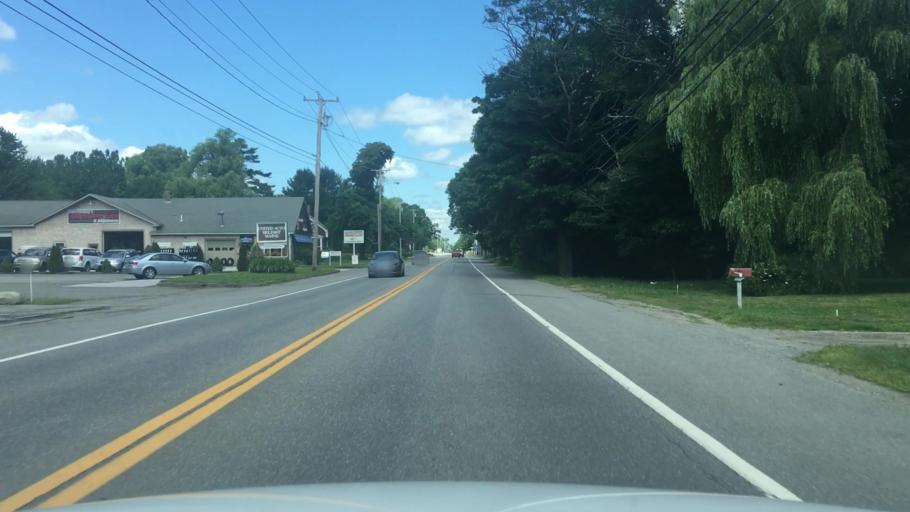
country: US
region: Maine
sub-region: Waldo County
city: Belfast
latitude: 44.4033
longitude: -68.9896
